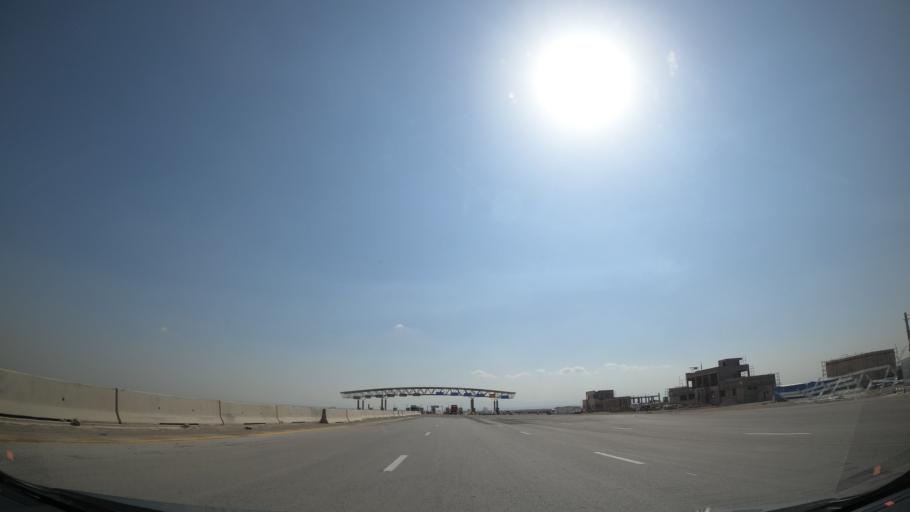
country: IR
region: Qazvin
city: Abyek
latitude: 35.9598
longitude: 50.4641
